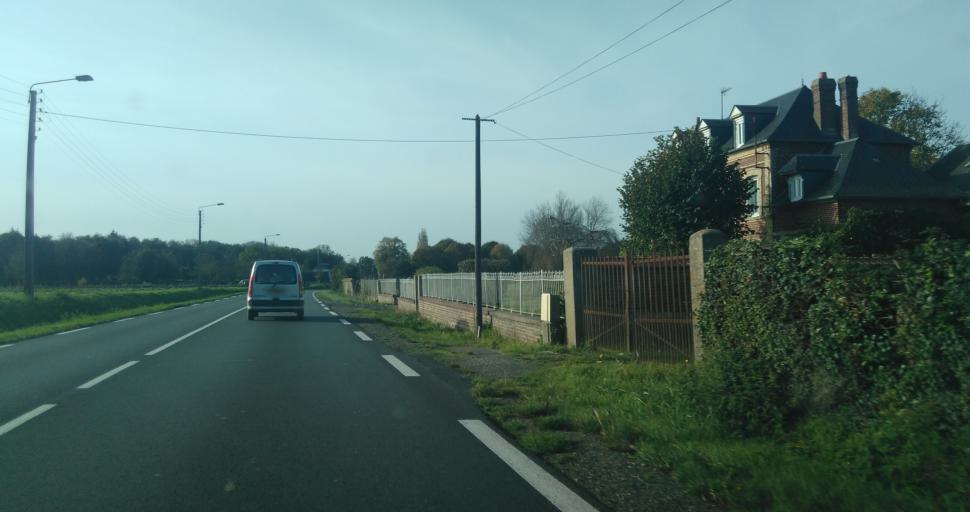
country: FR
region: Haute-Normandie
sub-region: Departement de l'Eure
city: Caumont
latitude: 49.3540
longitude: 0.9034
